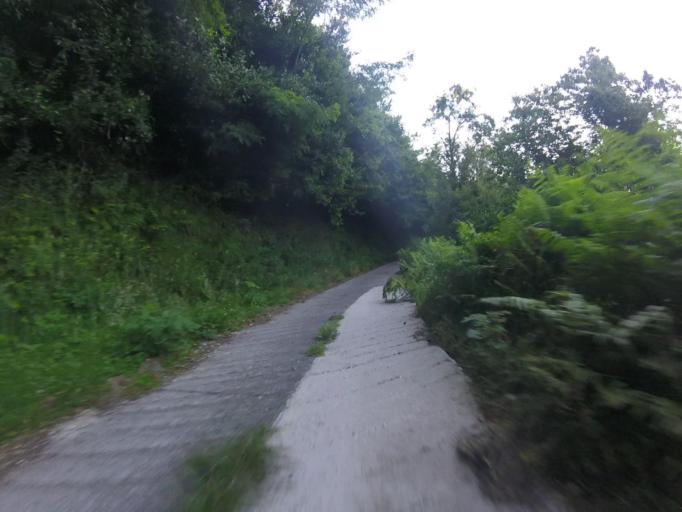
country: ES
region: Basque Country
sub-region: Provincia de Guipuzcoa
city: Irun
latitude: 43.3110
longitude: -1.7781
